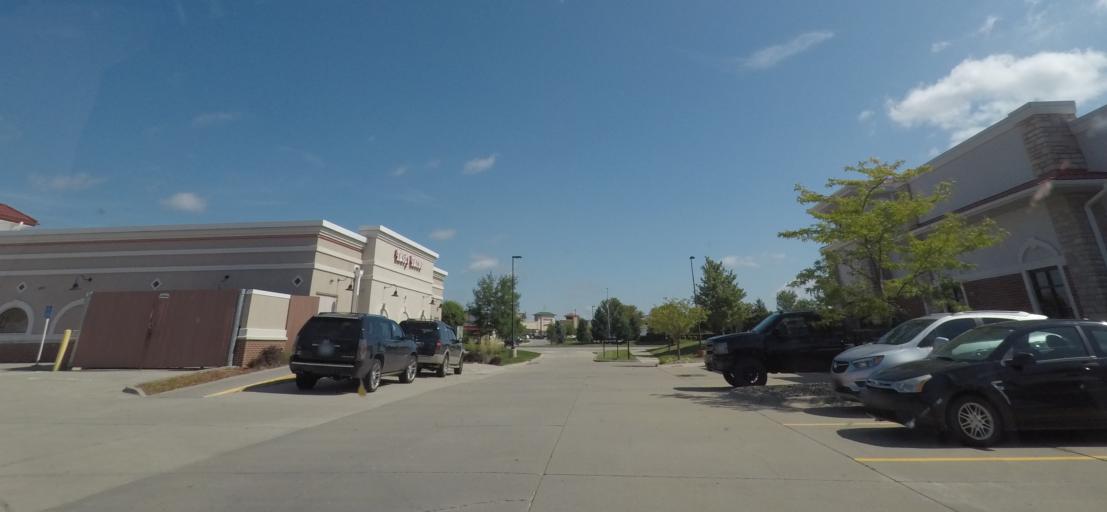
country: US
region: Iowa
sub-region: Polk County
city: Clive
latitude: 41.5601
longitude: -93.7960
